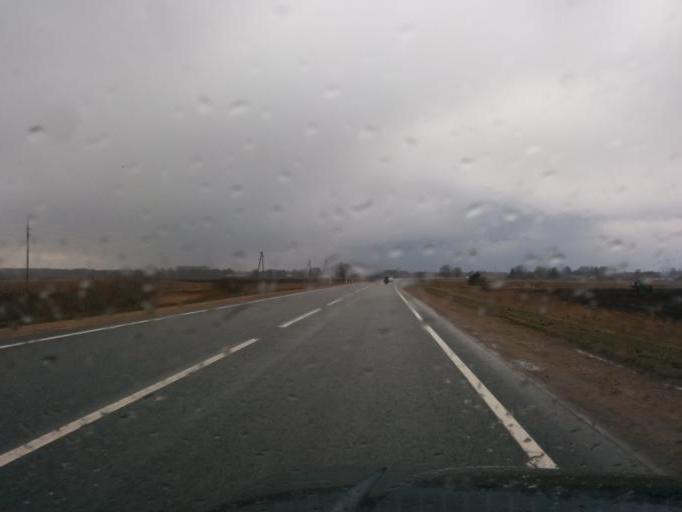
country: LV
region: Marupe
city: Marupe
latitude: 56.8648
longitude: 23.9761
